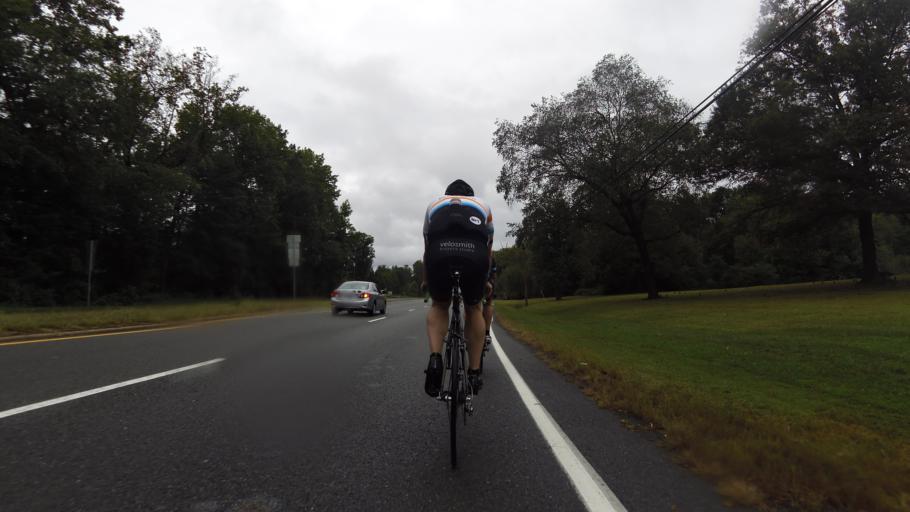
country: US
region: Virginia
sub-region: Henrico County
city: Tuckahoe
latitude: 37.5965
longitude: -77.5986
